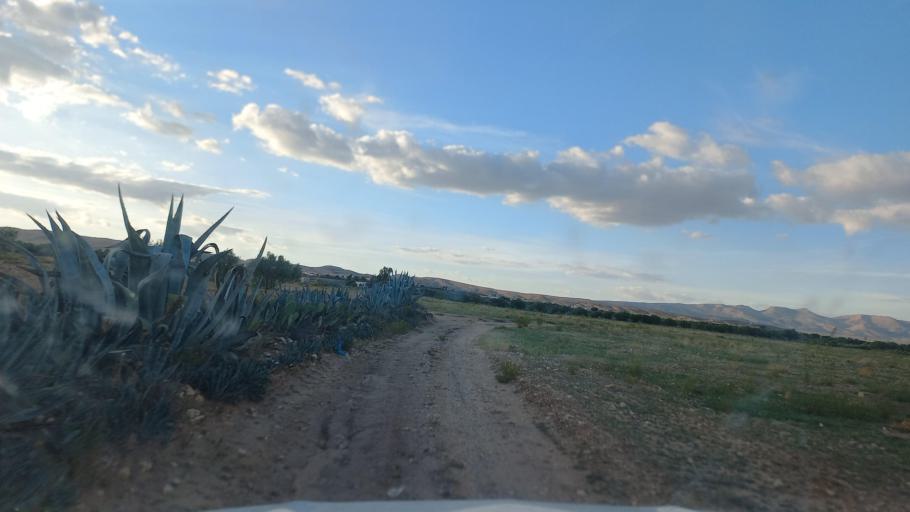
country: TN
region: Al Qasrayn
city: Sbiba
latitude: 35.3541
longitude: 9.0253
